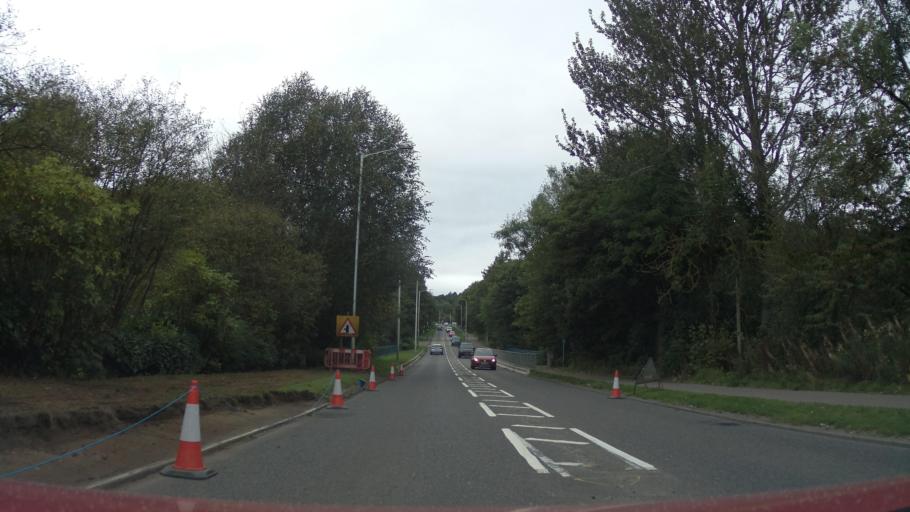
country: GB
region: Scotland
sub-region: Fife
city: Glenrothes
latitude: 56.2011
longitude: -3.1822
